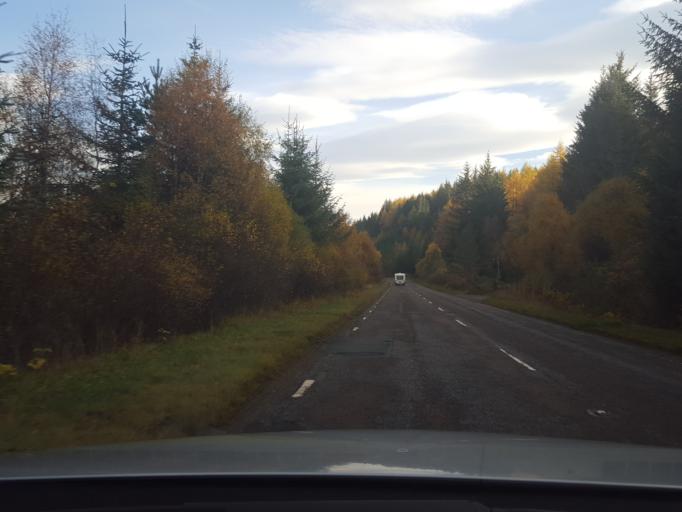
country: GB
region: Scotland
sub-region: Highland
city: Spean Bridge
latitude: 57.1687
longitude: -4.8407
